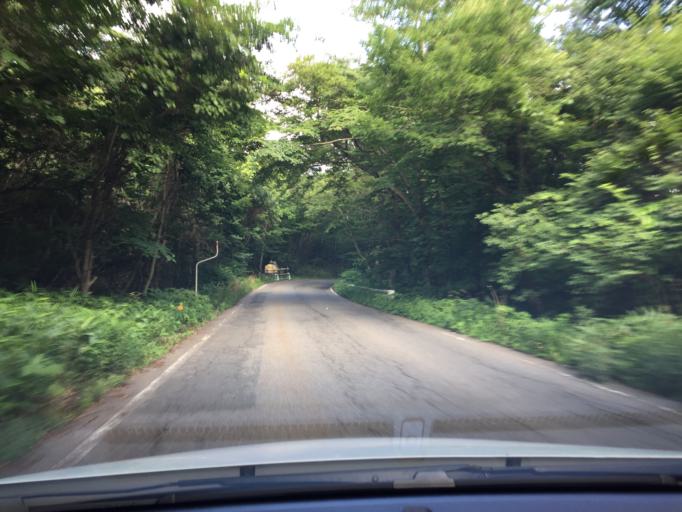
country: JP
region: Tochigi
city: Kuroiso
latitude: 37.2222
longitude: 140.0917
